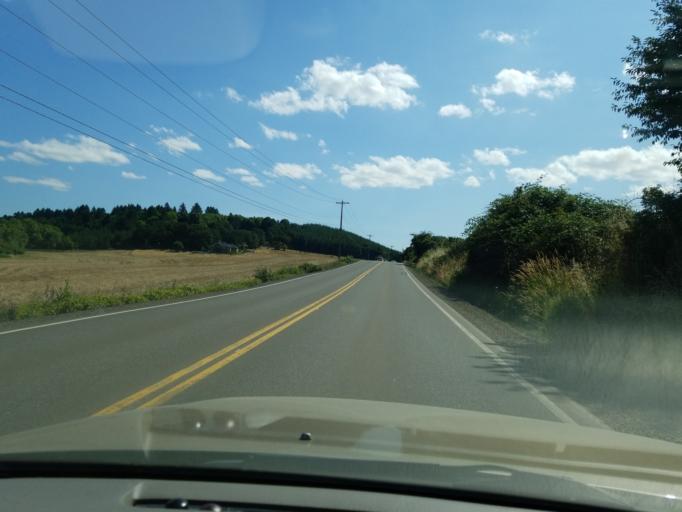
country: US
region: Oregon
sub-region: Yamhill County
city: Lafayette
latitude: 45.3072
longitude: -123.0928
